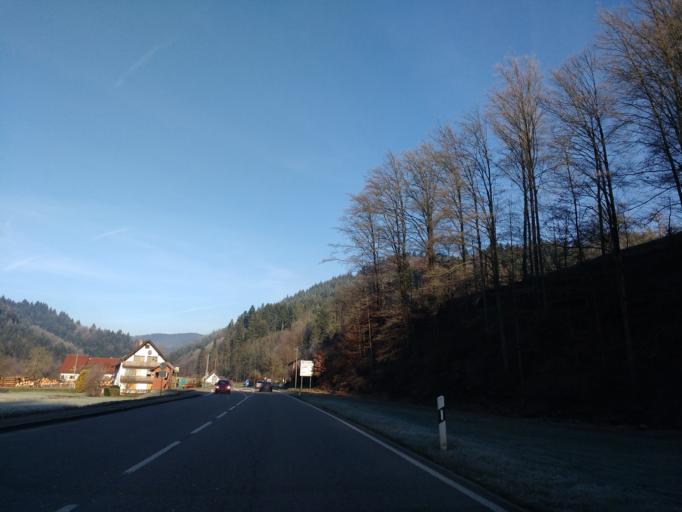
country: DE
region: Baden-Wuerttemberg
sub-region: Freiburg Region
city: Oppenau
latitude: 48.4945
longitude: 8.1419
